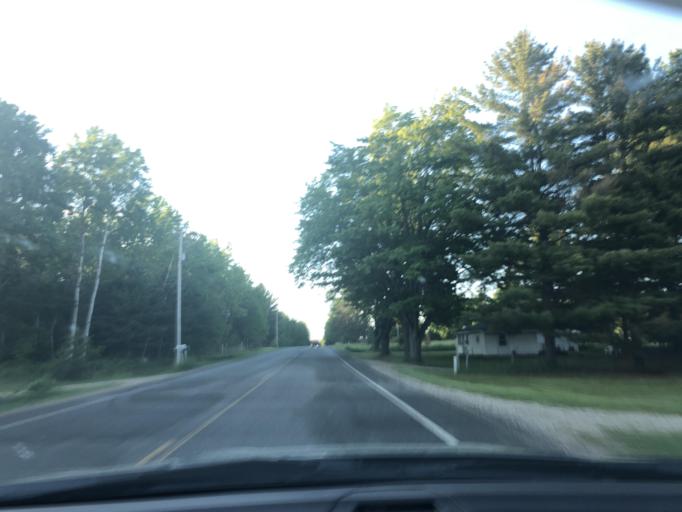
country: US
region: Michigan
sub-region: Missaukee County
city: Lake City
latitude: 44.3856
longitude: -85.0758
